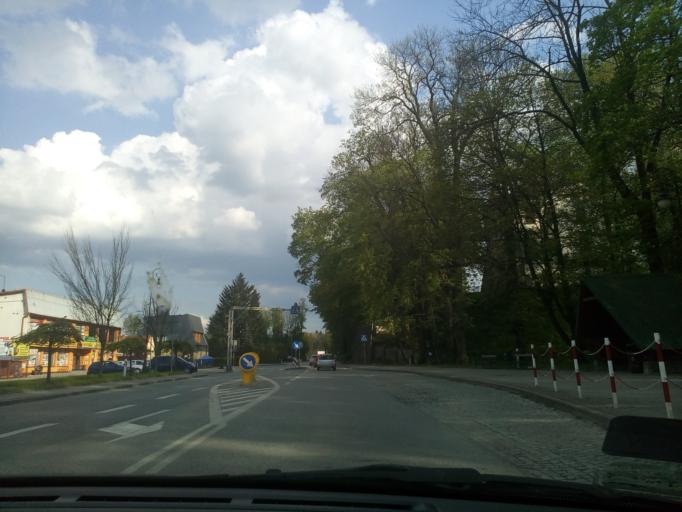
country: PL
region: Lesser Poland Voivodeship
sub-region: Powiat nowosadecki
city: Nawojowa
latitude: 49.5606
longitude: 20.7446
